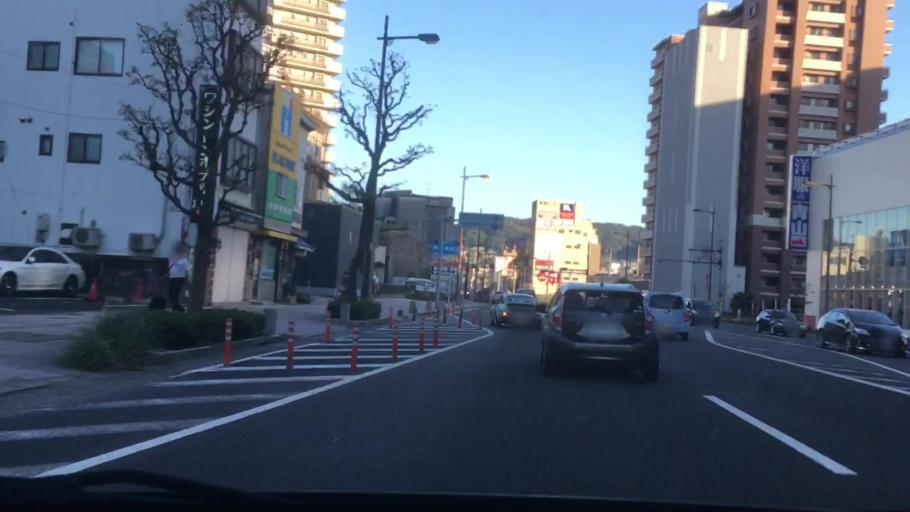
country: JP
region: Nagasaki
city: Sasebo
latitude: 33.1634
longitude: 129.7280
